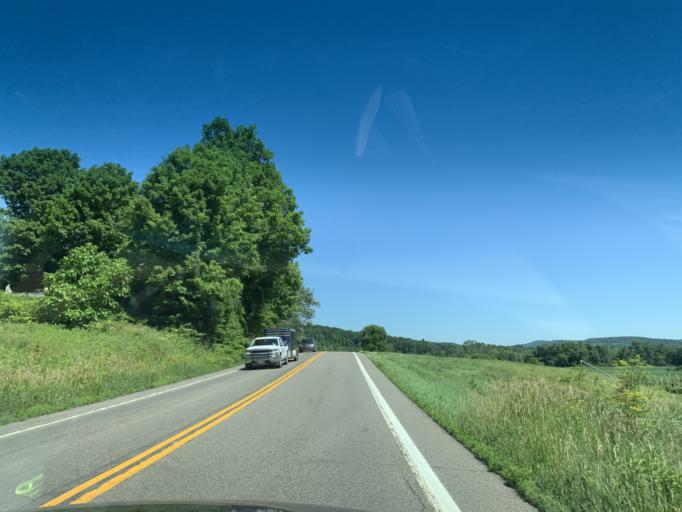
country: US
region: New York
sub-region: Chenango County
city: Norwich
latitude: 42.5039
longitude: -75.4043
